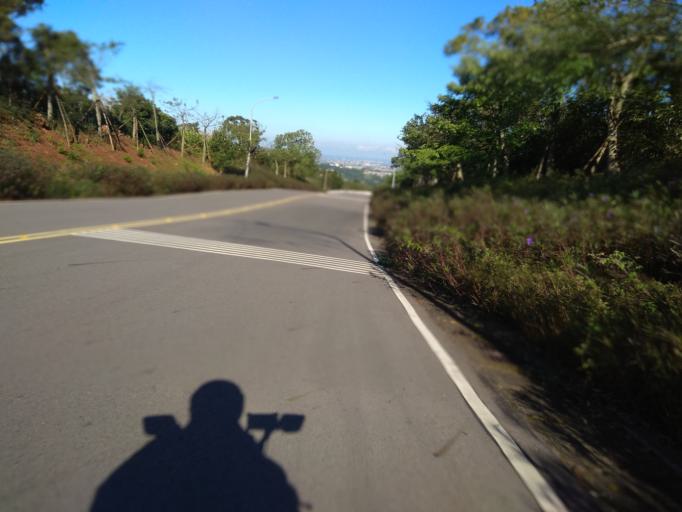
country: TW
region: Taiwan
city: Daxi
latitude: 24.8907
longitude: 121.1482
